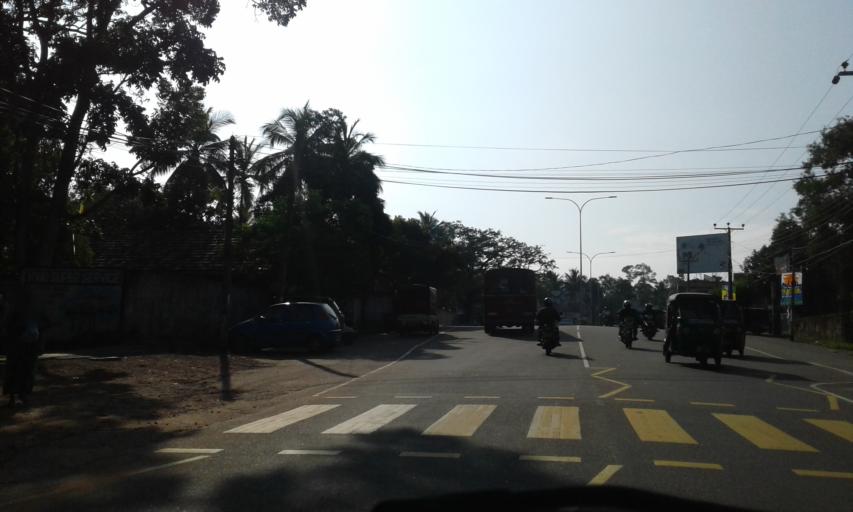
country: LK
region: Western
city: Gampaha
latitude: 7.0744
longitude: 80.0151
